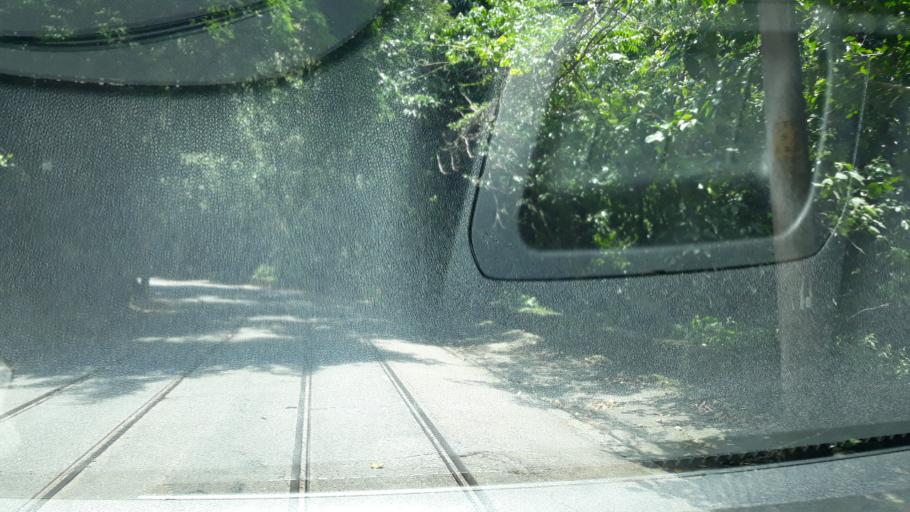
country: BR
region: Rio de Janeiro
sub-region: Rio De Janeiro
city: Rio de Janeiro
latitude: -22.9421
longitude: -43.2092
